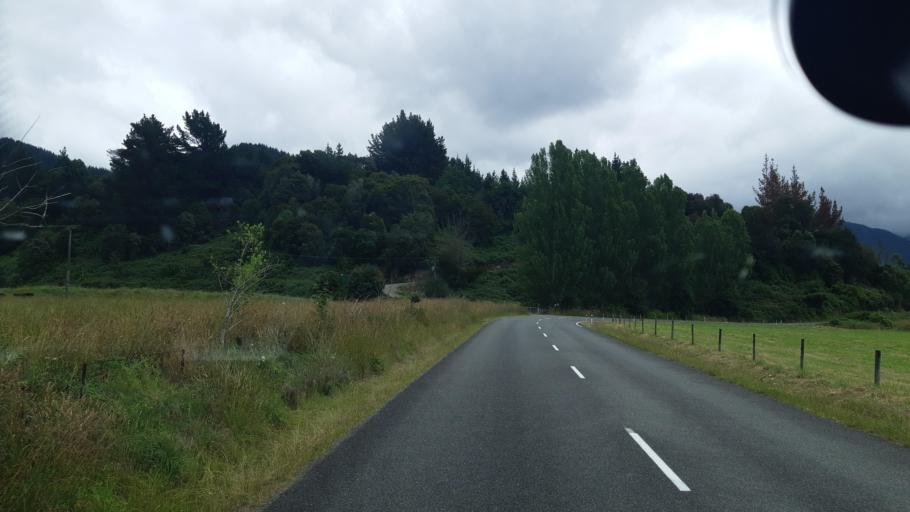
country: NZ
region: Marlborough
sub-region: Marlborough District
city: Blenheim
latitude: -41.4741
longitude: 173.7375
